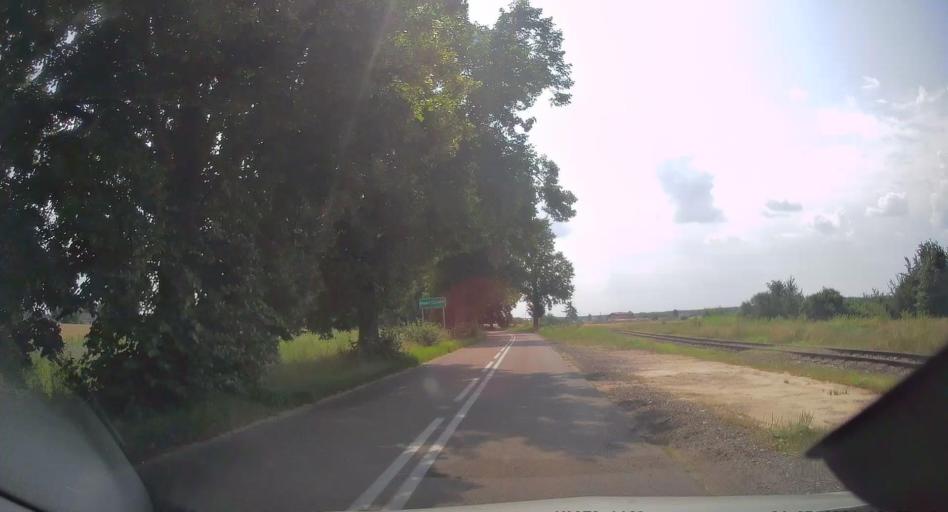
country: PL
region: Lodz Voivodeship
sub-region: Powiat tomaszowski
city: Lubochnia
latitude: 51.5704
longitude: 20.1004
